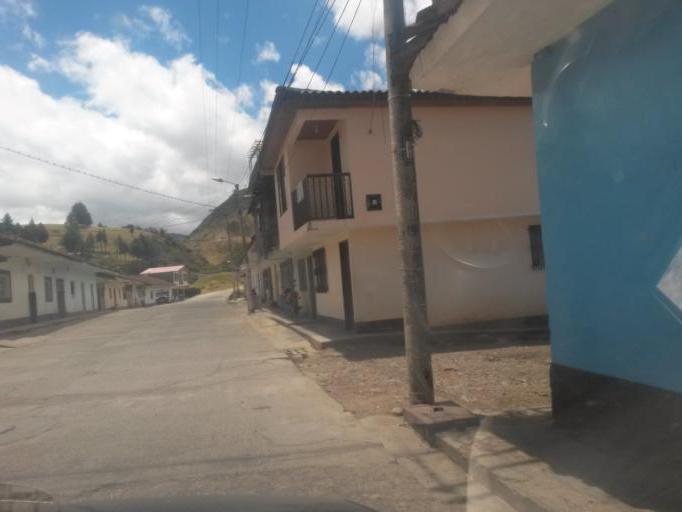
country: CO
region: Cauca
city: Silvia
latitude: 2.6157
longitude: -76.3720
